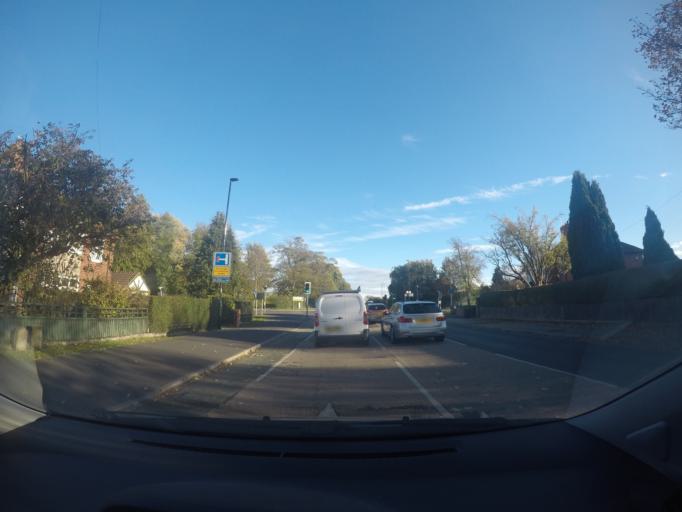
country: GB
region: England
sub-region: City of York
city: Nether Poppleton
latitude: 53.9702
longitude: -1.1341
